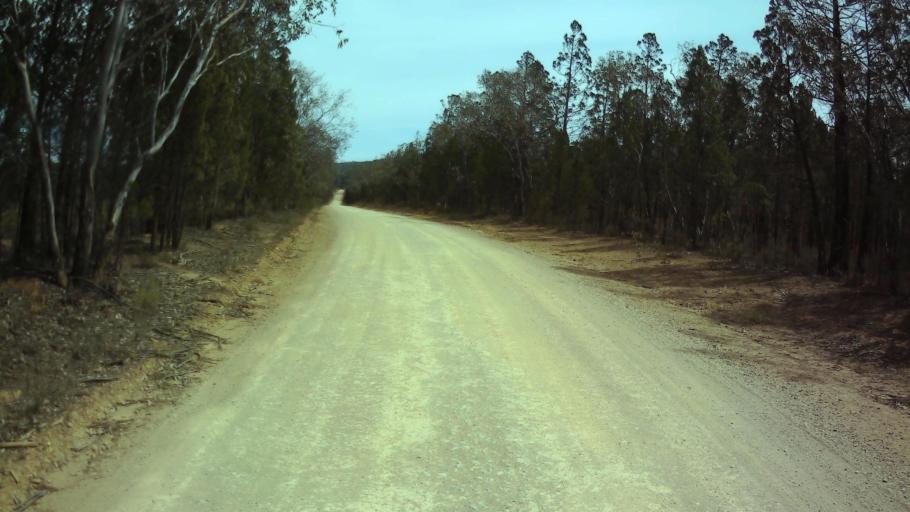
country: AU
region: New South Wales
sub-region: Weddin
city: Grenfell
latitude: -33.9113
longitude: 148.4124
